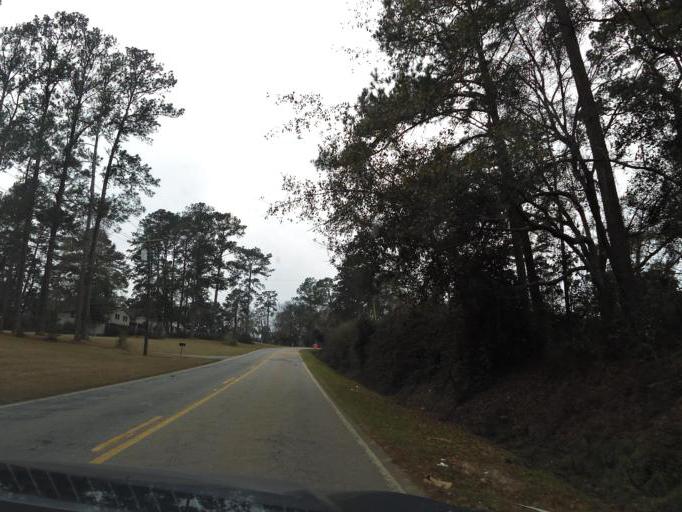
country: US
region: Georgia
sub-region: Thomas County
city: Thomasville
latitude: 30.8123
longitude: -83.9549
